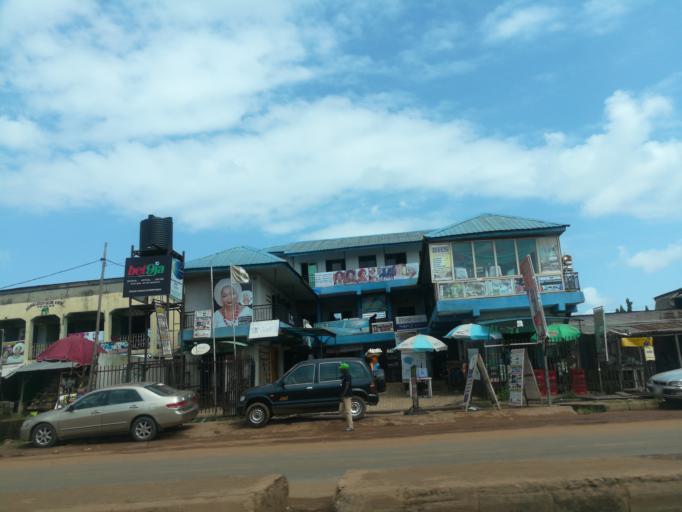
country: NG
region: Oyo
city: Ibadan
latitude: 7.4214
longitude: 3.9743
